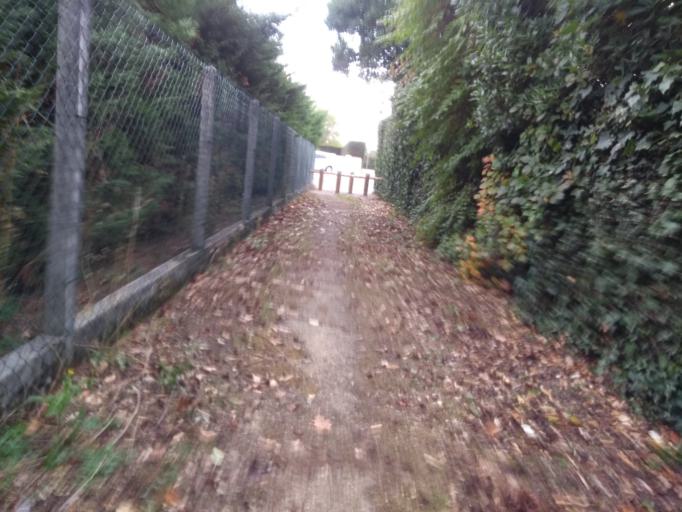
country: FR
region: Aquitaine
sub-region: Departement de la Gironde
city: Cestas
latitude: 44.7340
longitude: -0.6645
